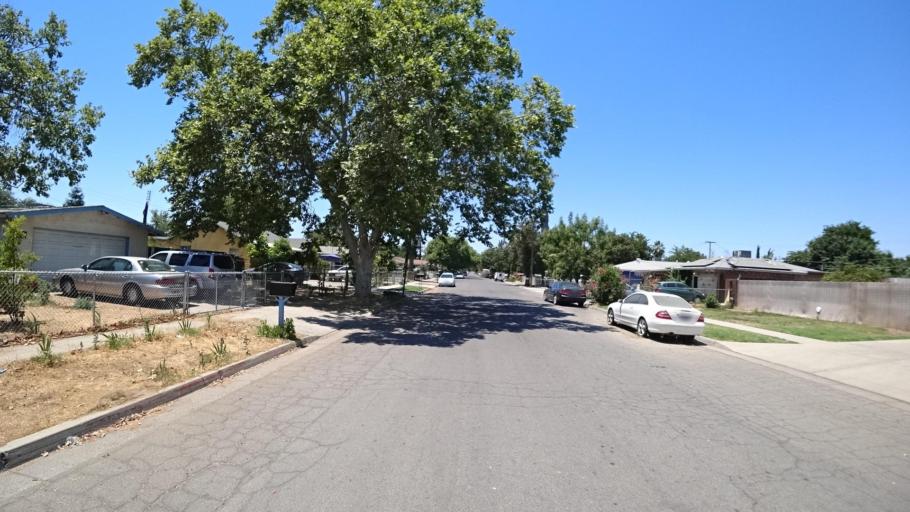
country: US
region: California
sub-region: Fresno County
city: West Park
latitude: 36.7240
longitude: -119.8224
